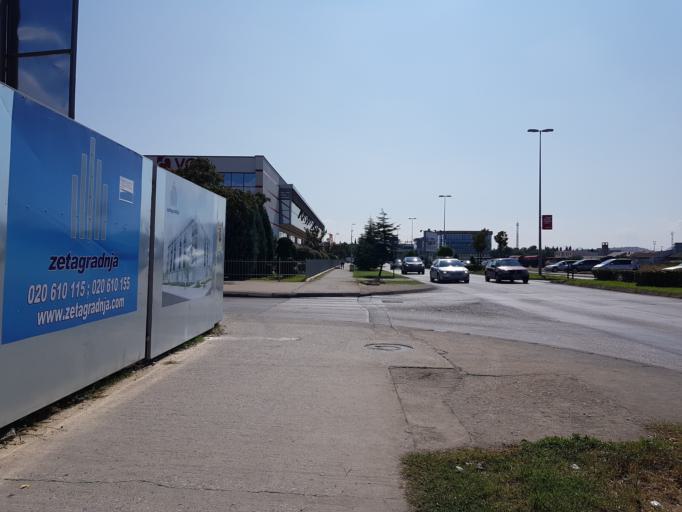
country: ME
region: Podgorica
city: Podgorica
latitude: 42.4296
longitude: 19.2720
